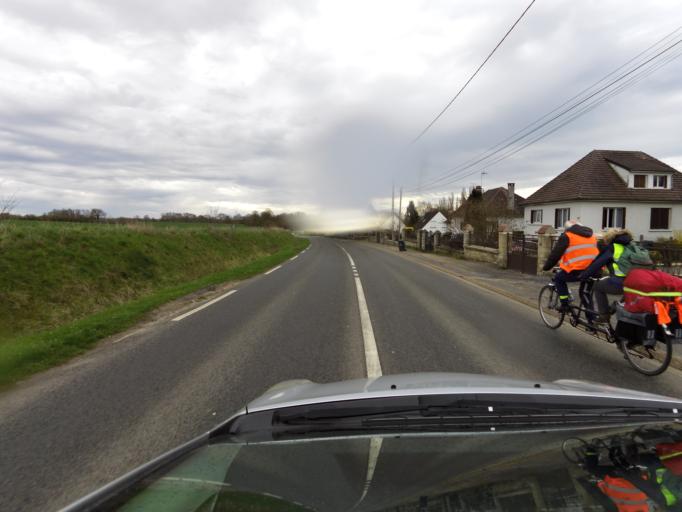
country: FR
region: Picardie
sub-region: Departement de l'Oise
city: Chamant
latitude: 49.1940
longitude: 2.6363
